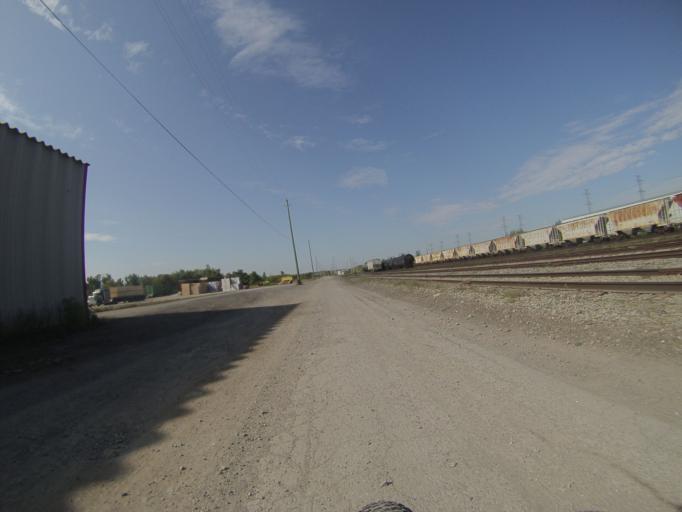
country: CA
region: Ontario
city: Ottawa
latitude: 45.3685
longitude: -75.6442
